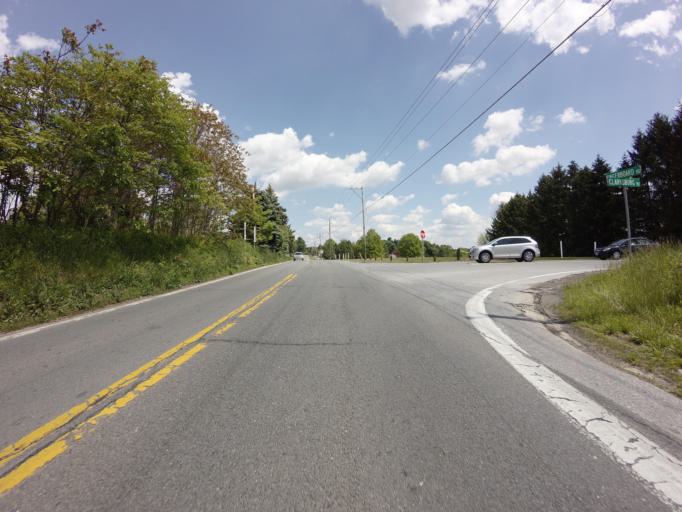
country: US
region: Maryland
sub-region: Montgomery County
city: Damascus
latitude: 39.3354
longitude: -77.2259
